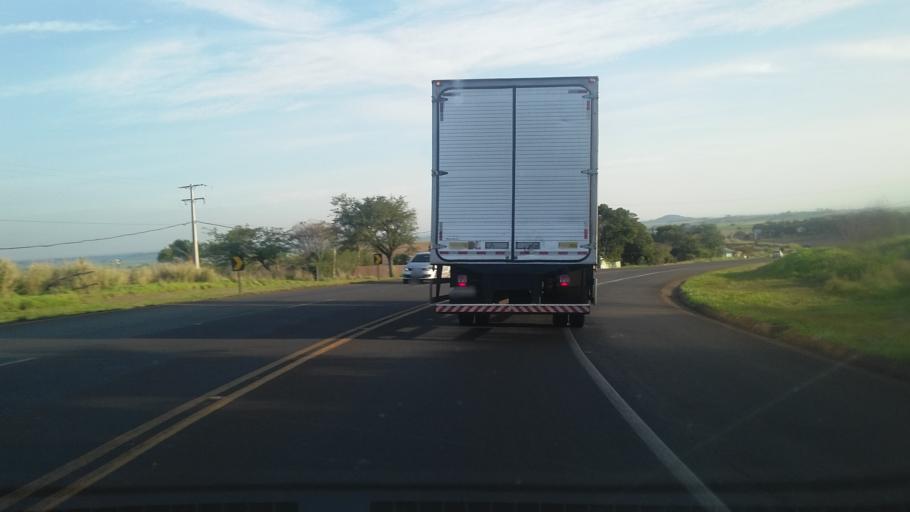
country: BR
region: Parana
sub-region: Bandeirantes
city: Bandeirantes
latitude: -23.1700
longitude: -50.6131
